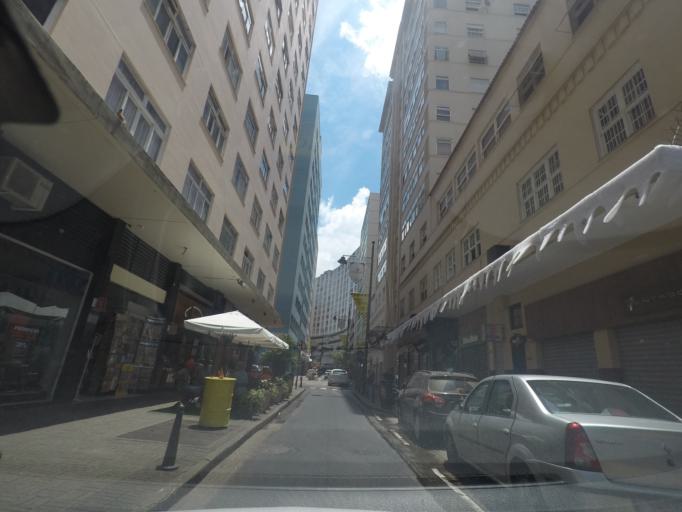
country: BR
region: Rio de Janeiro
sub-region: Petropolis
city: Petropolis
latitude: -22.5104
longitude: -43.1778
